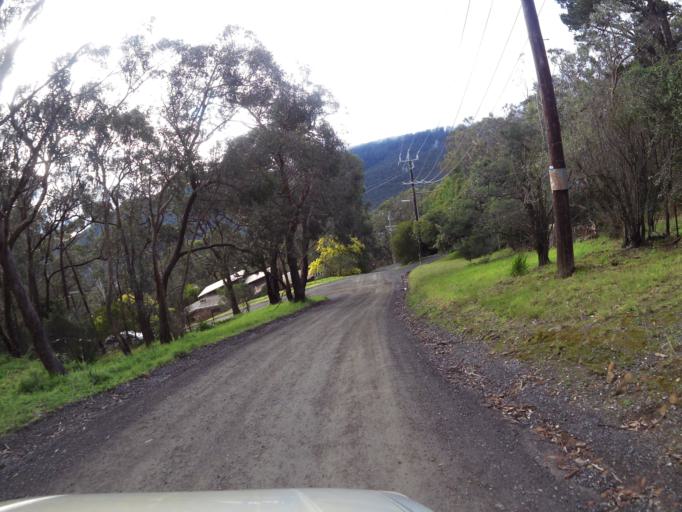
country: AU
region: Victoria
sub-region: Yarra Ranges
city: Tremont
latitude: -37.9036
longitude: 145.3185
